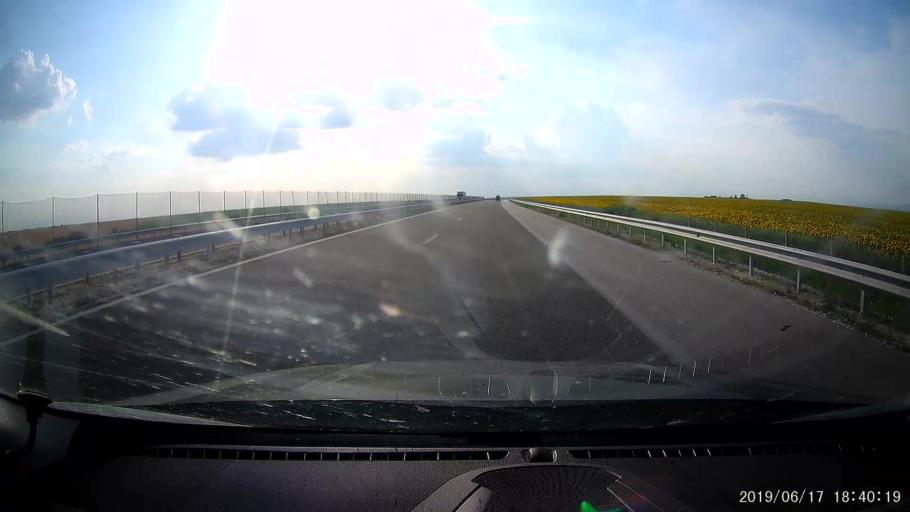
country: BG
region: Stara Zagora
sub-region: Obshtina Chirpan
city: Chirpan
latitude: 42.1541
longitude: 25.2809
